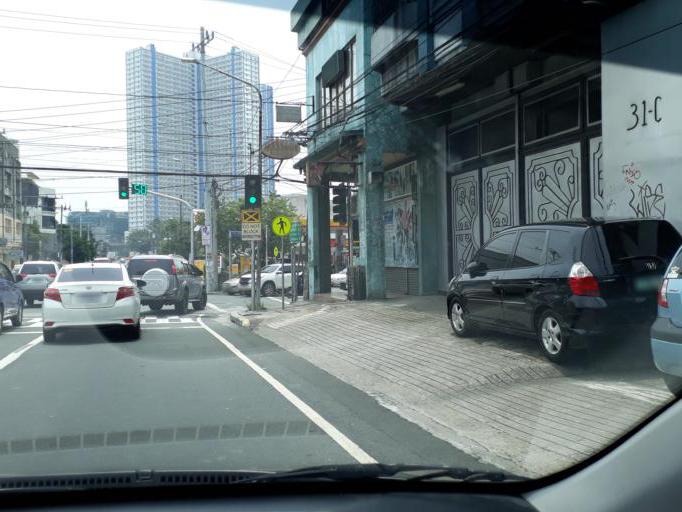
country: PH
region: Calabarzon
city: Del Monte
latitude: 14.6182
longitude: 121.0059
